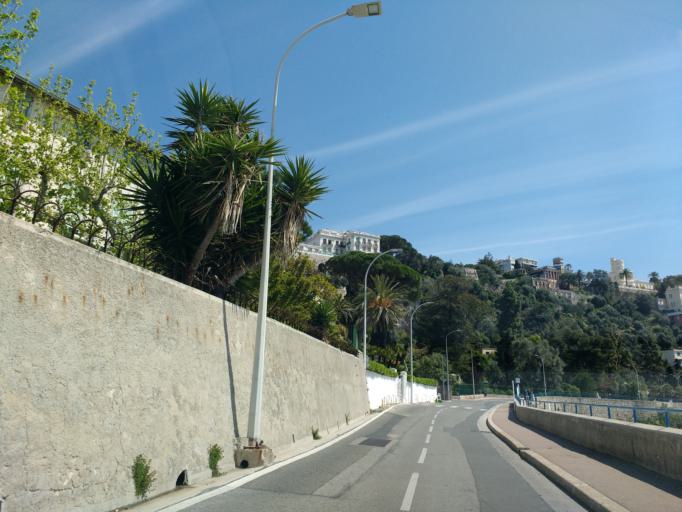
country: FR
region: Provence-Alpes-Cote d'Azur
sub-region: Departement des Alpes-Maritimes
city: Villefranche-sur-Mer
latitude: 43.6913
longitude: 7.2928
